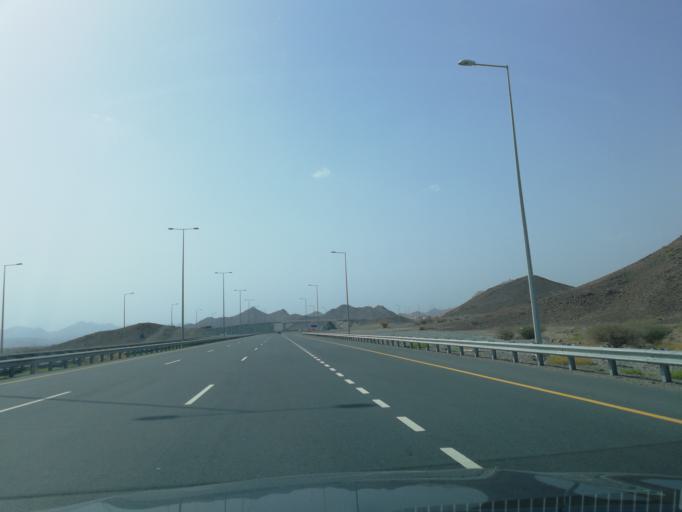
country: OM
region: Ash Sharqiyah
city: Ibra'
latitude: 22.9083
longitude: 58.2670
